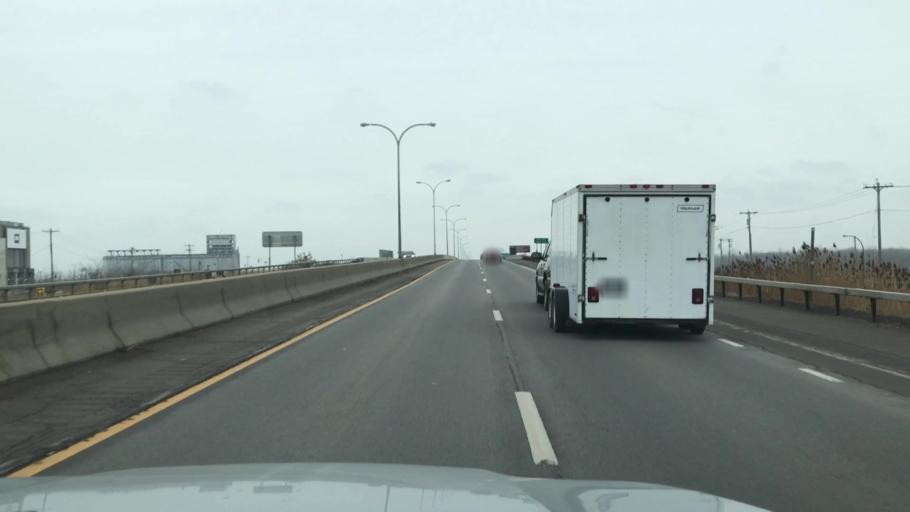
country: US
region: New York
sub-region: Erie County
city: Lackawanna
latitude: 42.8326
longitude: -78.8532
